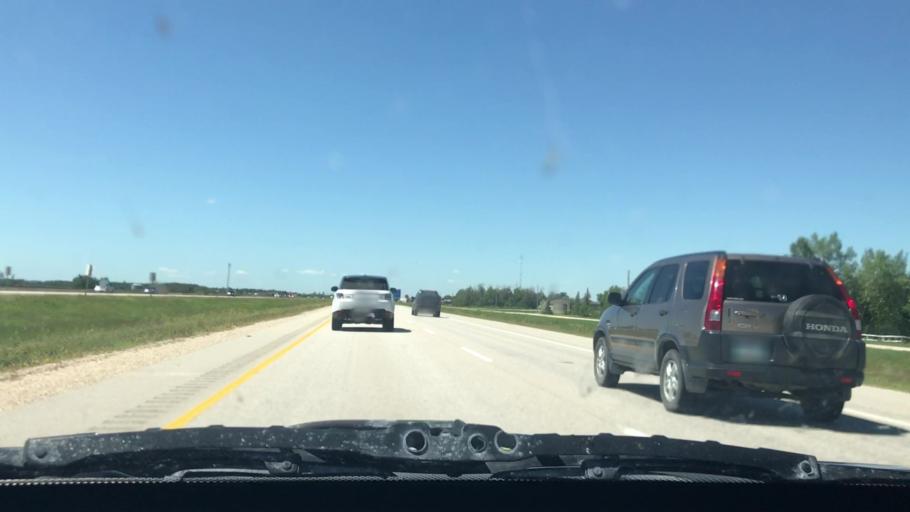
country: CA
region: Manitoba
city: Winnipeg
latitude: 49.8144
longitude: -96.9213
